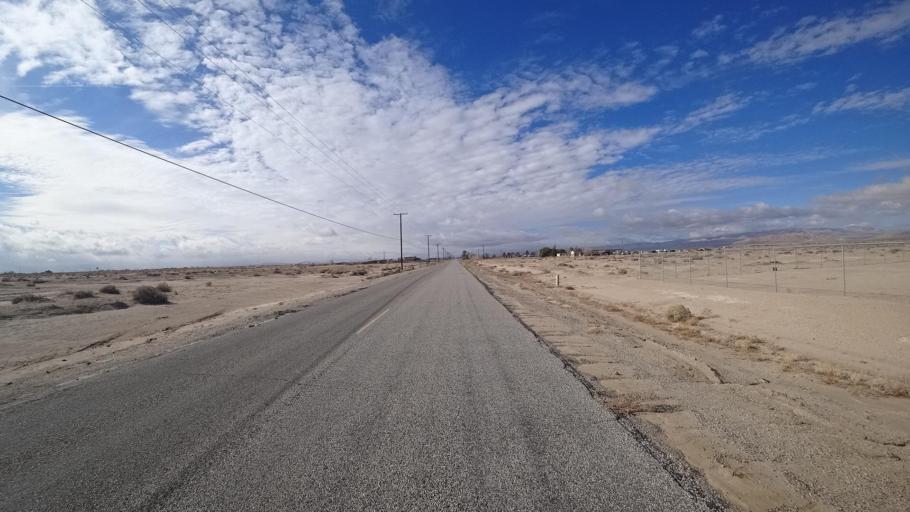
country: US
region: California
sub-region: Kern County
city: Rosamond
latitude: 34.8202
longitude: -118.2064
